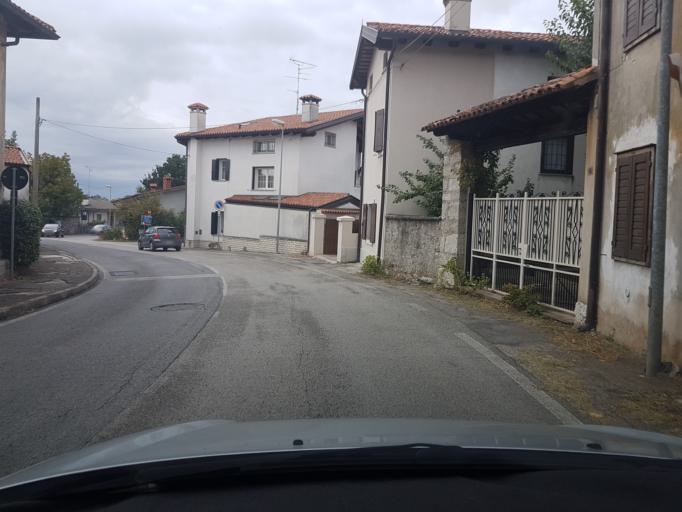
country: IT
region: Friuli Venezia Giulia
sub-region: Provincia di Gorizia
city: Doberdo del Lago
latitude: 45.8430
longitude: 13.5391
